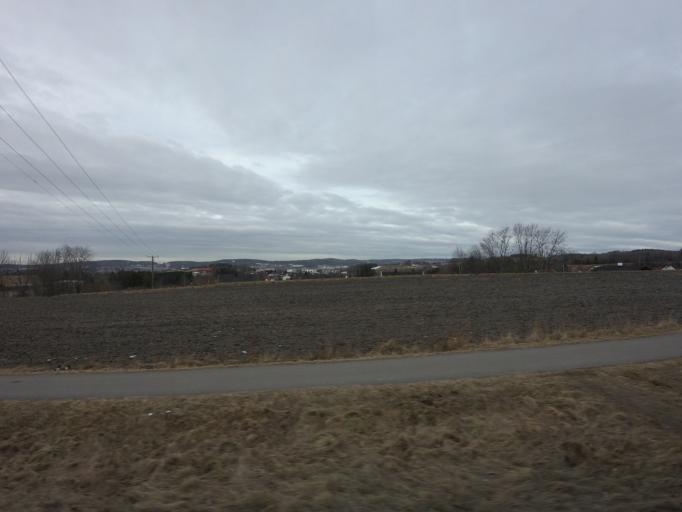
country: NO
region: Akershus
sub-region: Skedsmo
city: Lillestrom
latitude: 59.9874
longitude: 11.0479
